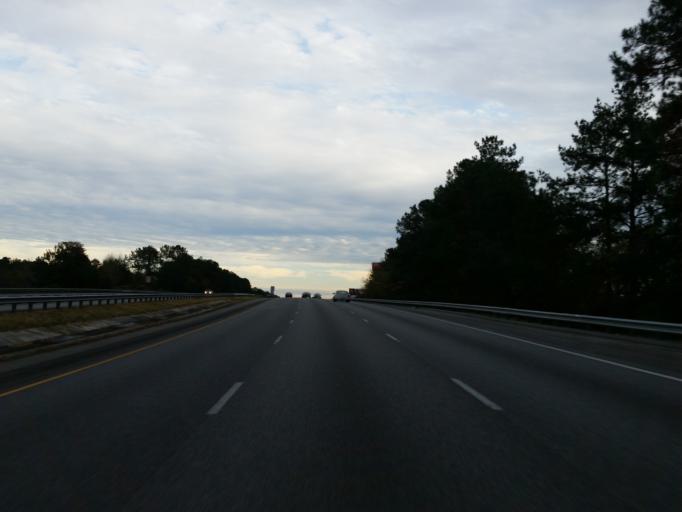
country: US
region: Georgia
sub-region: Lowndes County
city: Valdosta
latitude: 30.7732
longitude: -83.2935
